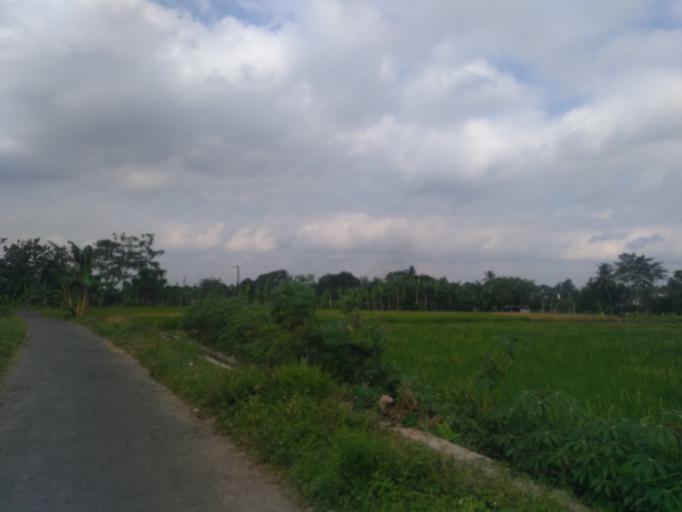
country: ID
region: Daerah Istimewa Yogyakarta
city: Yogyakarta
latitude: -7.7629
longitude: 110.3528
